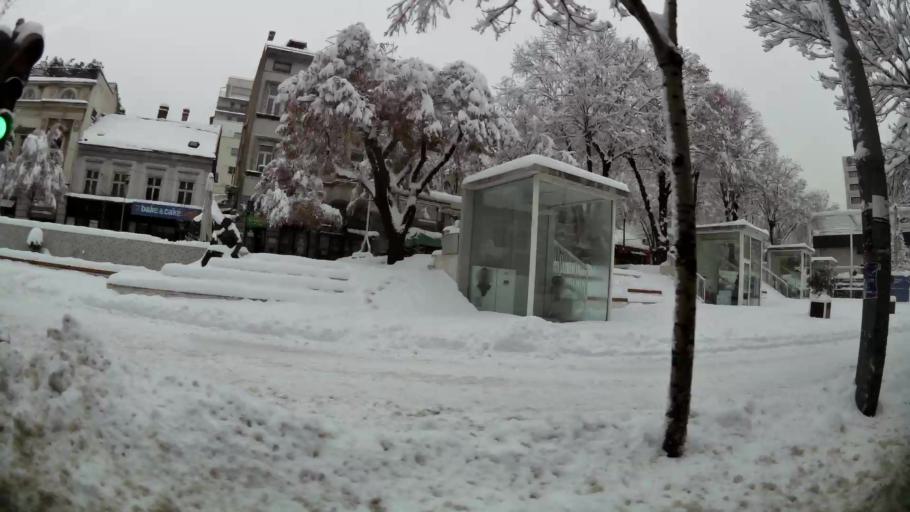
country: RS
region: Central Serbia
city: Belgrade
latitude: 44.8058
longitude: 20.4650
